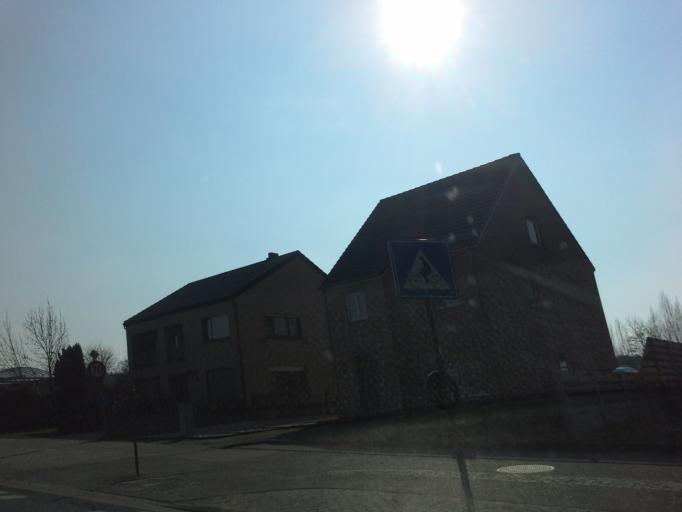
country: BE
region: Flanders
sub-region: Provincie Limburg
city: Tessenderlo
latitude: 51.0842
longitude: 5.1056
